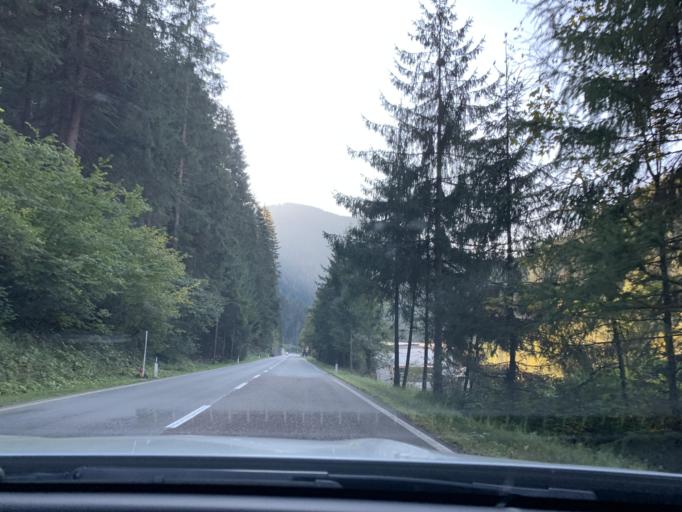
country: IT
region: Trentino-Alto Adige
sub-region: Bolzano
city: Nova Levante
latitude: 46.4254
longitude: 11.4946
